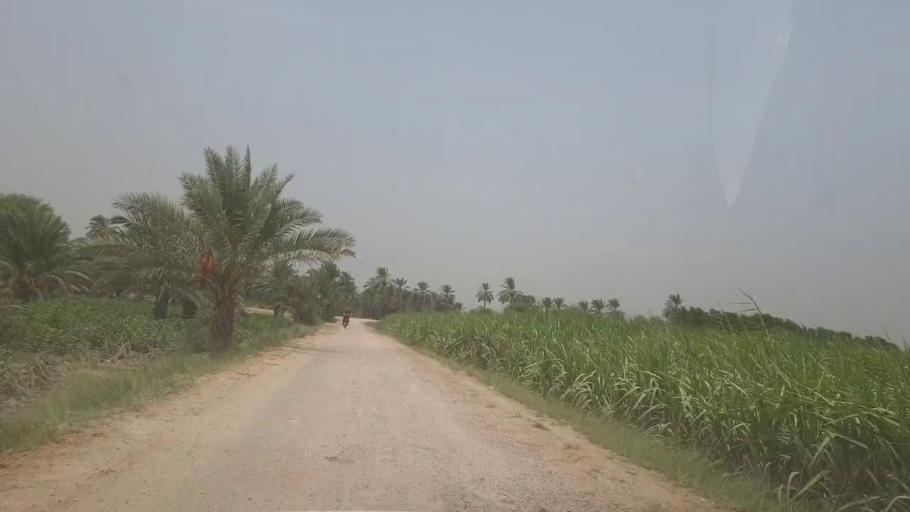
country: PK
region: Sindh
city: Kot Diji
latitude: 27.4426
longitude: 68.6403
